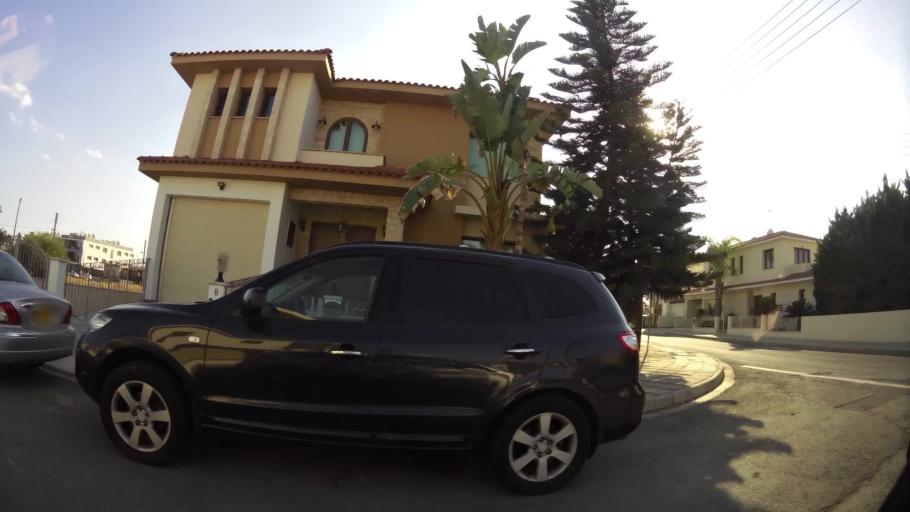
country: CY
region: Larnaka
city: Aradippou
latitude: 34.9431
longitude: 33.6004
